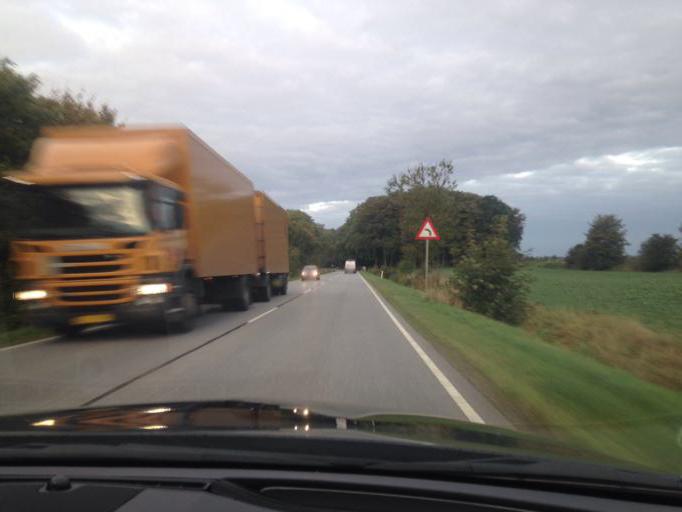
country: DK
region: South Denmark
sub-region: Haderslev Kommune
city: Vojens
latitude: 55.2559
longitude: 9.3359
